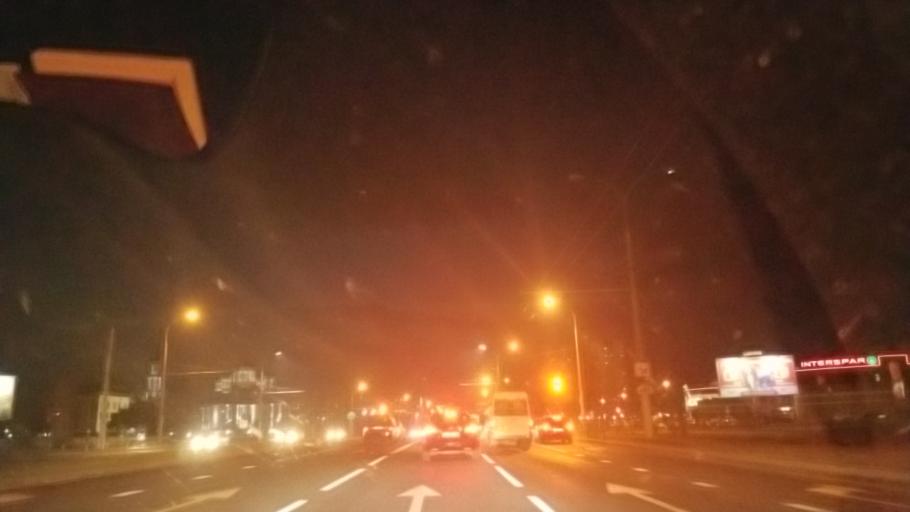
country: BY
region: Brest
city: Brest
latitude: 52.0953
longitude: 23.7664
